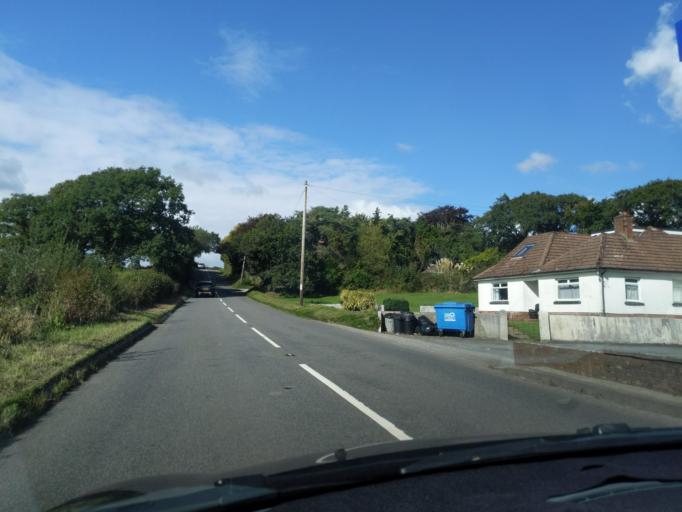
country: GB
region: England
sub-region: Devon
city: Holsworthy
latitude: 50.7933
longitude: -4.3400
